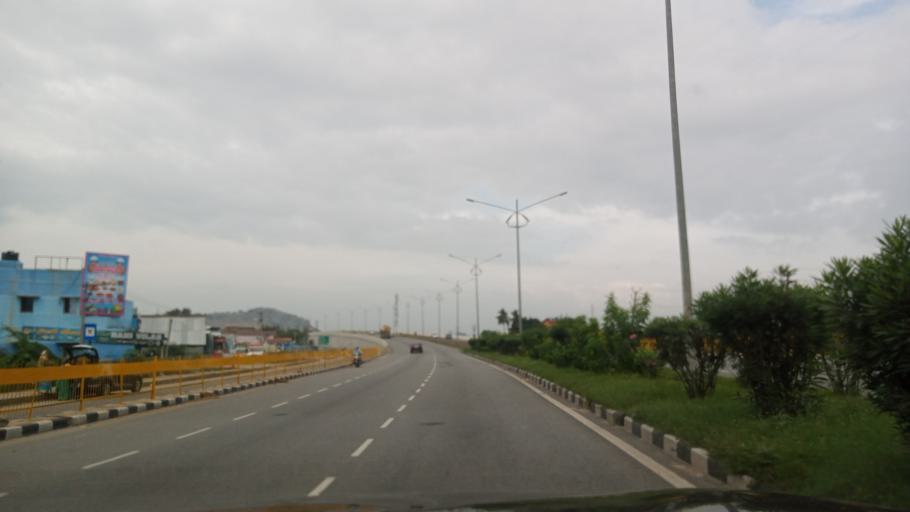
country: IN
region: Tamil Nadu
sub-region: Krishnagiri
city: Krishnagiri
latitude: 12.5117
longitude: 78.2288
